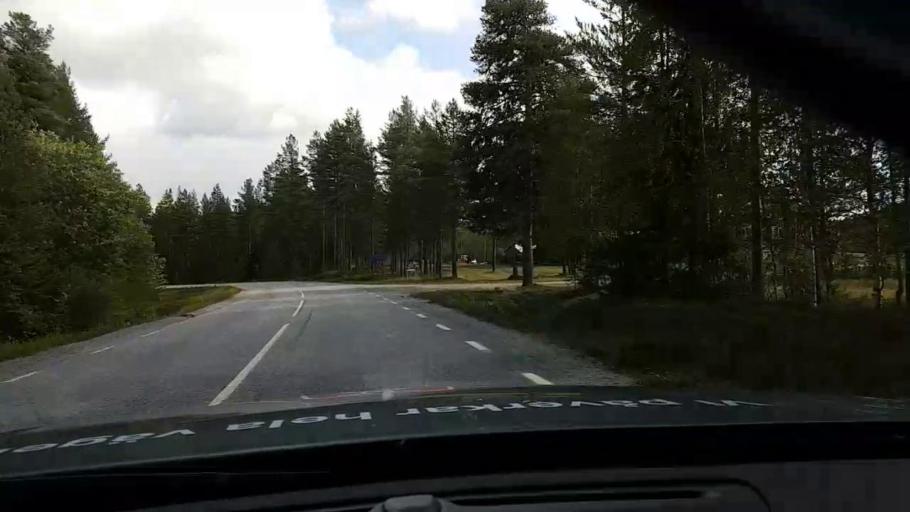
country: SE
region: Vaesternorrland
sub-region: OErnskoeldsviks Kommun
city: Bredbyn
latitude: 63.6738
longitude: 17.8000
